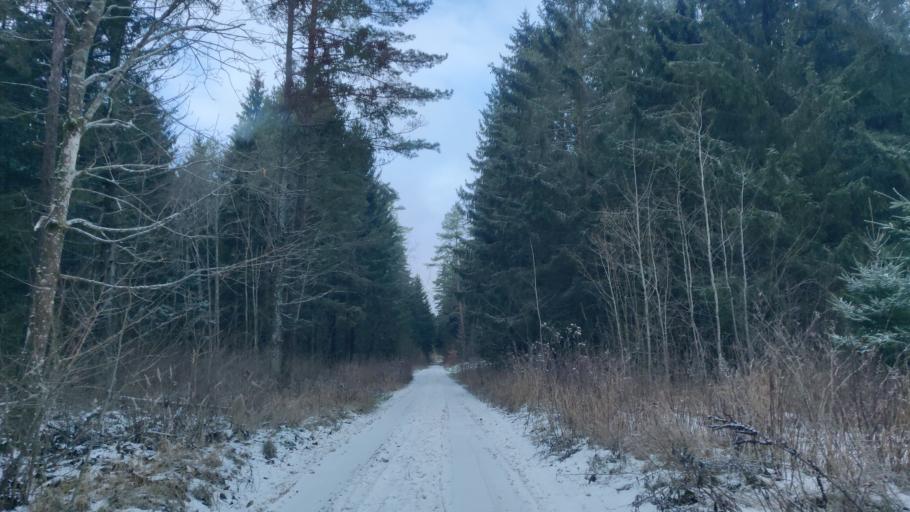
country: LT
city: Trakai
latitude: 54.5813
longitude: 24.9673
